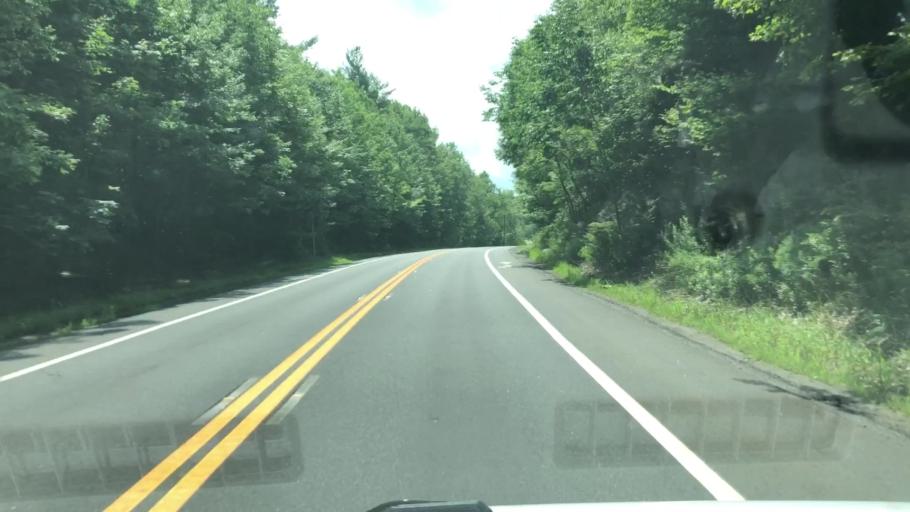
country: US
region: Massachusetts
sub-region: Franklin County
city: Ashfield
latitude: 42.5168
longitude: -72.8068
